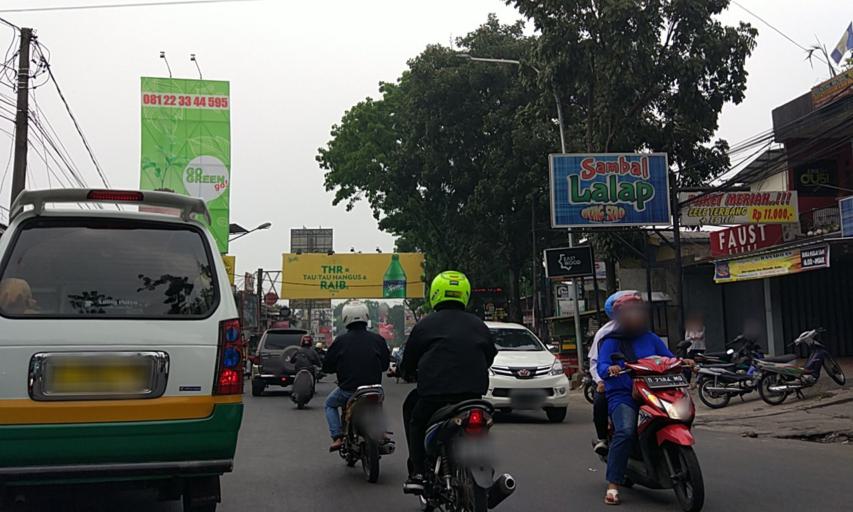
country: ID
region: West Java
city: Bandung
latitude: -6.8908
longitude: 107.6169
